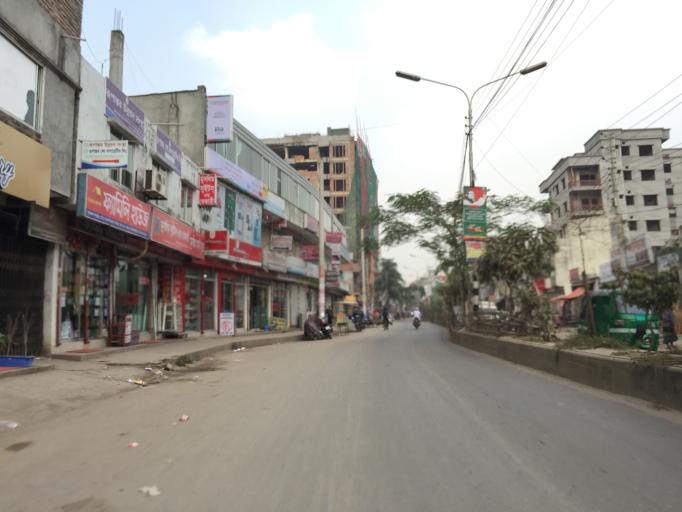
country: BD
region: Dhaka
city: Azimpur
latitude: 23.7926
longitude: 90.3653
